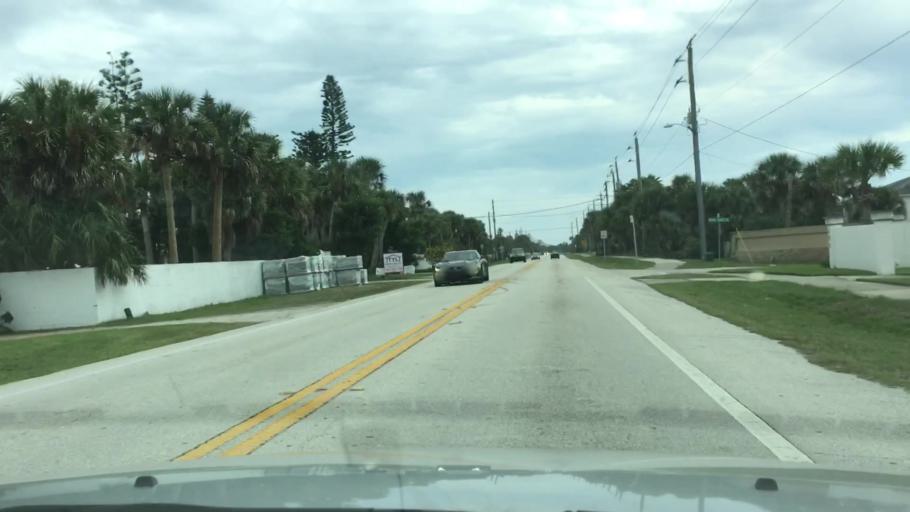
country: US
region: Florida
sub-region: Volusia County
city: Ormond Beach
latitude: 29.3089
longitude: -81.0484
